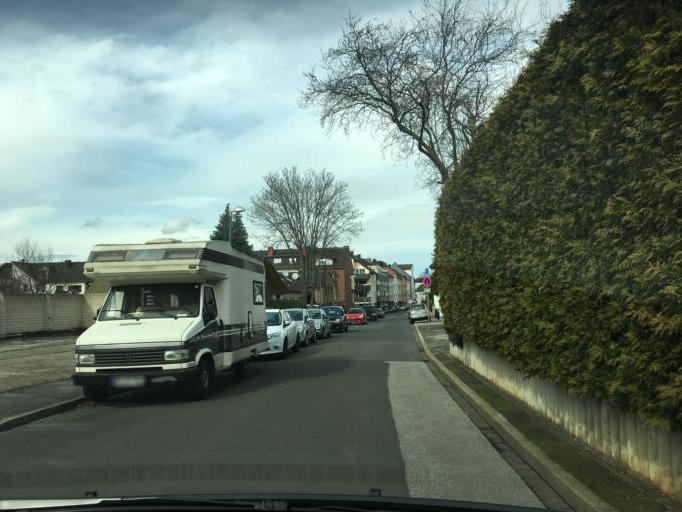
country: DE
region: North Rhine-Westphalia
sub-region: Regierungsbezirk Koln
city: Dueren
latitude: 50.7994
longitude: 6.4936
